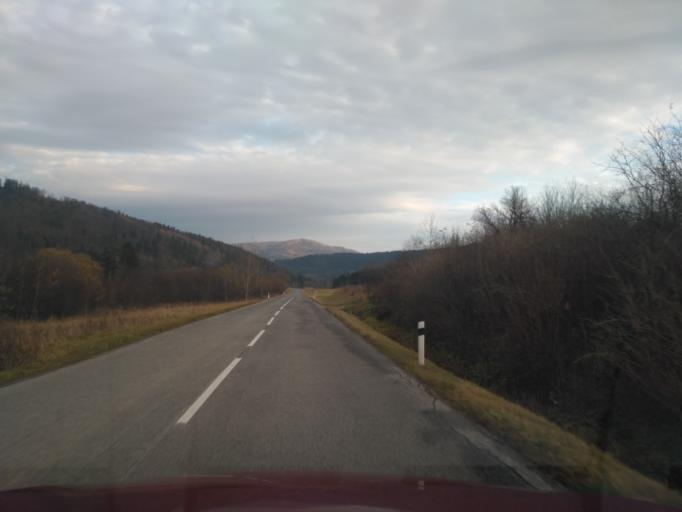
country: SK
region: Kosicky
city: Krompachy
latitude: 48.8011
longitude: 20.7340
